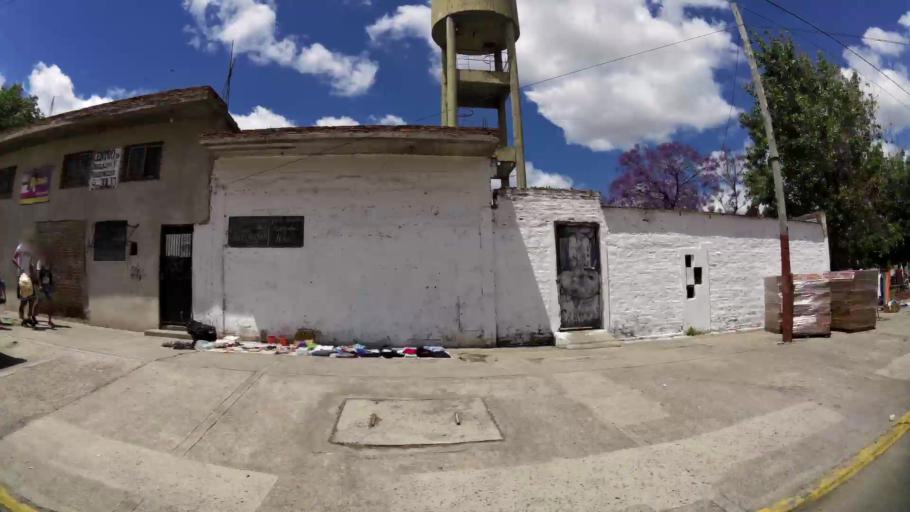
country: AR
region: Buenos Aires
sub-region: Partido de Lanus
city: Lanus
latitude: -34.6987
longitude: -58.4315
